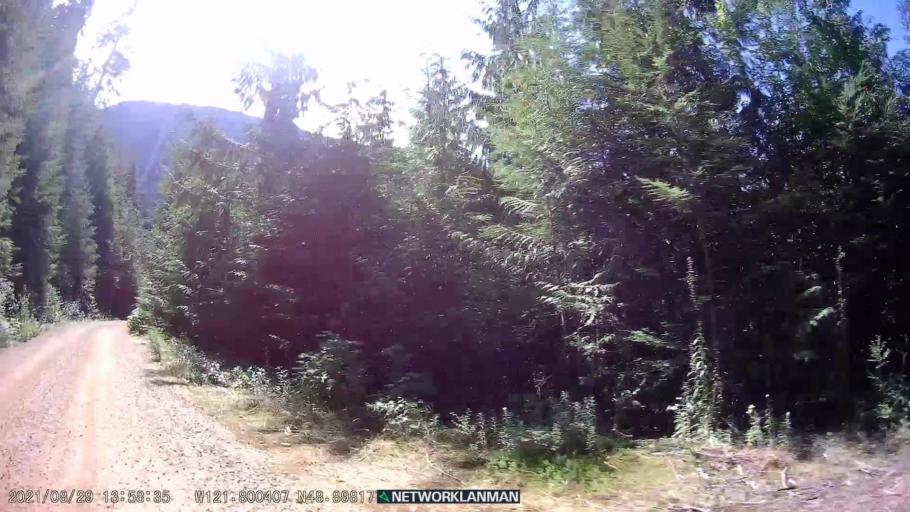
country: CA
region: British Columbia
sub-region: Fraser Valley Regional District
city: Chilliwack
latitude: 48.8979
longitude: -121.8004
